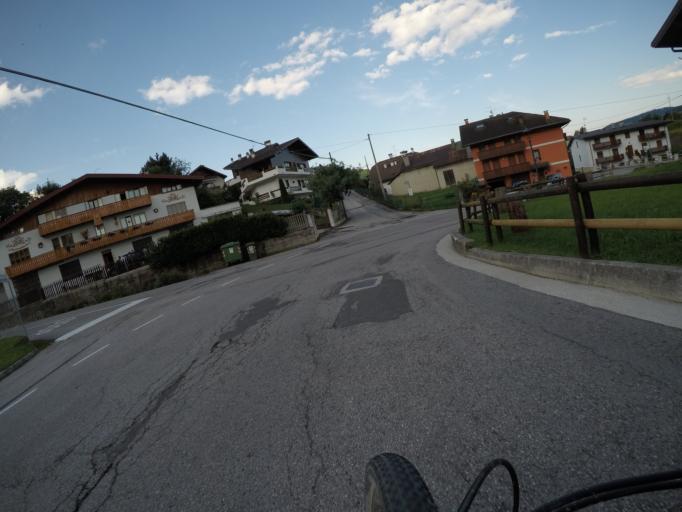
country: IT
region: Veneto
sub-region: Provincia di Vicenza
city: Gallio
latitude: 45.8934
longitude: 11.5416
